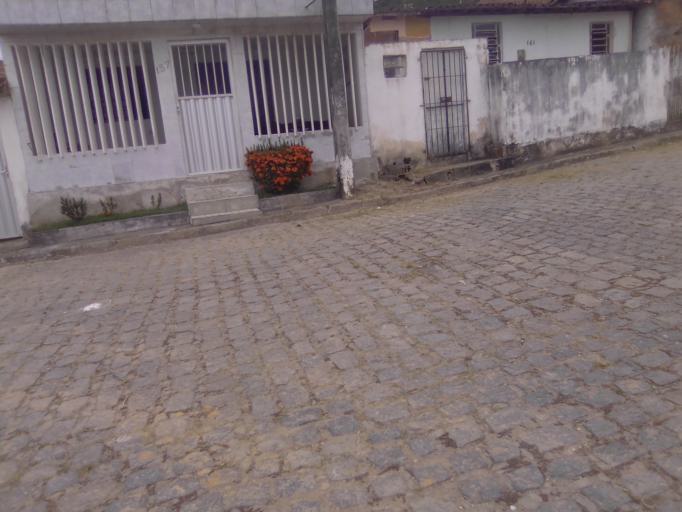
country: BR
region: Pernambuco
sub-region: Jaboatao Dos Guararapes
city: Jaboatao dos Guararapes
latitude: -8.0655
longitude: -35.0030
